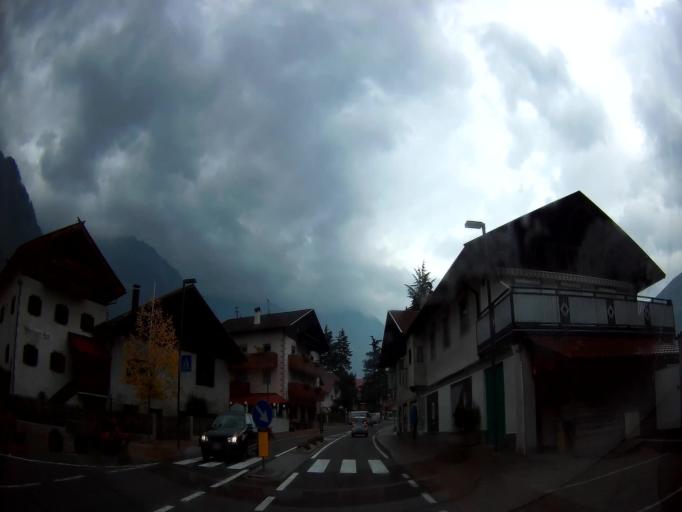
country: IT
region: Trentino-Alto Adige
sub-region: Bolzano
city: Rabla
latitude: 46.6693
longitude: 11.0601
